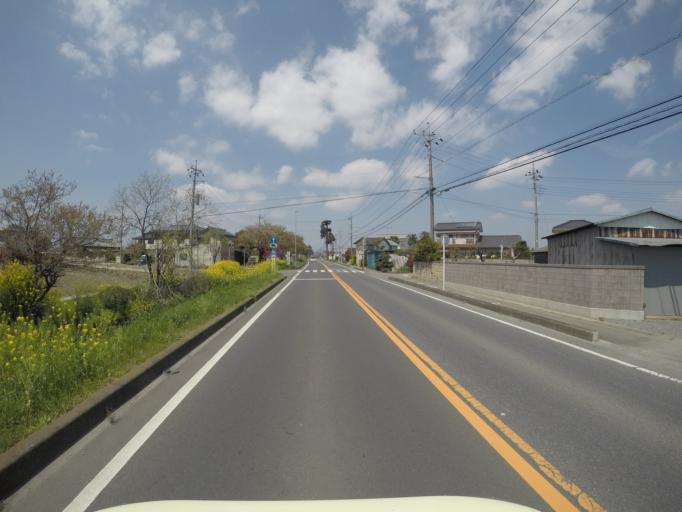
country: JP
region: Tochigi
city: Mibu
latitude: 36.4388
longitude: 139.7885
